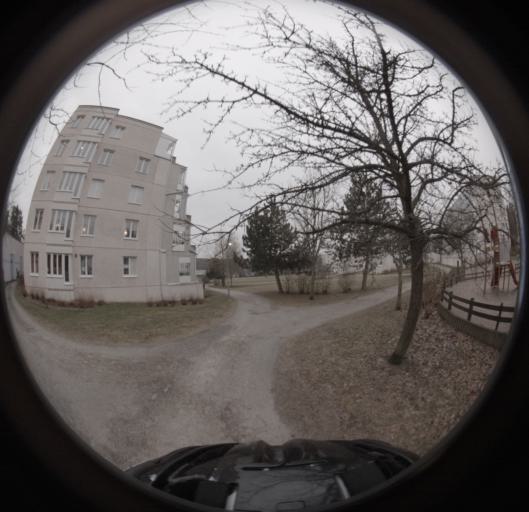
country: SE
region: Stockholm
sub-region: Upplands Vasby Kommun
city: Upplands Vaesby
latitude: 59.4854
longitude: 17.9356
